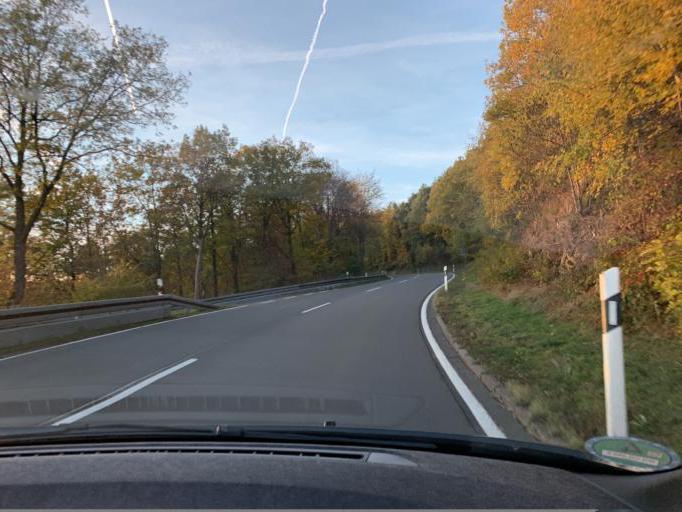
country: DE
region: North Rhine-Westphalia
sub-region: Regierungsbezirk Koln
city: Simmerath
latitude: 50.5927
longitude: 6.3599
